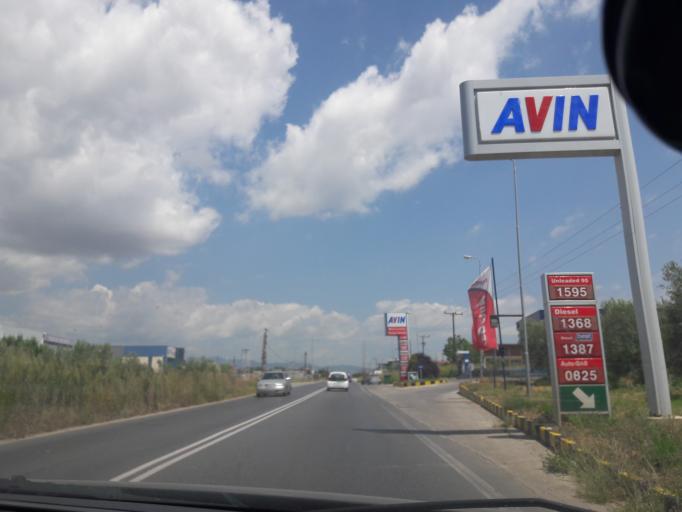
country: GR
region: Central Macedonia
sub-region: Nomos Chalkidikis
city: Nea Moudhania
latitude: 40.2508
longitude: 23.3148
